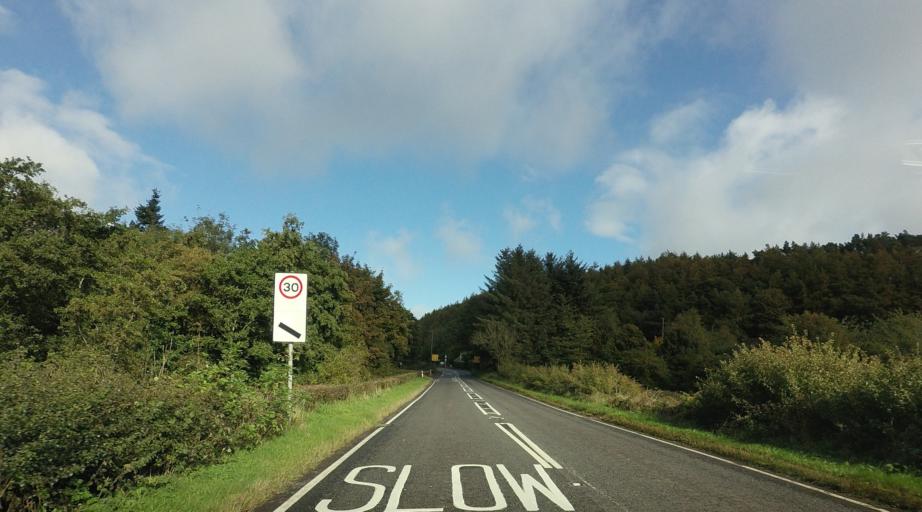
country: GB
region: Scotland
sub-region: Fife
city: Balmullo
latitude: 56.3896
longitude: -2.9090
